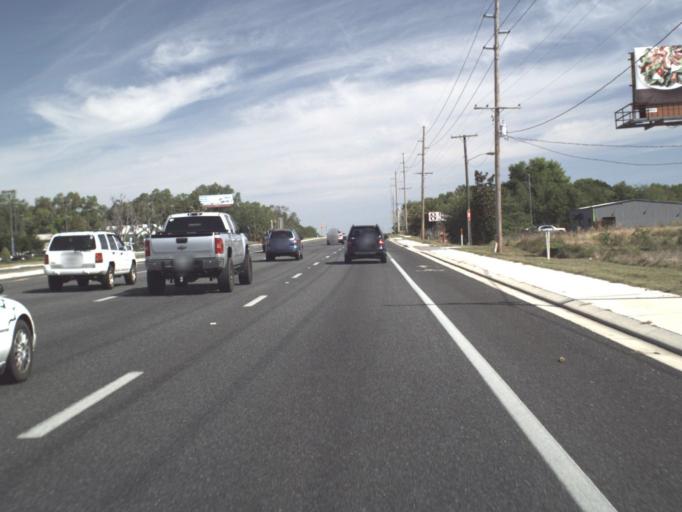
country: US
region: Florida
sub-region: Lake County
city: Fruitland Park
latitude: 28.8809
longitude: -81.9063
